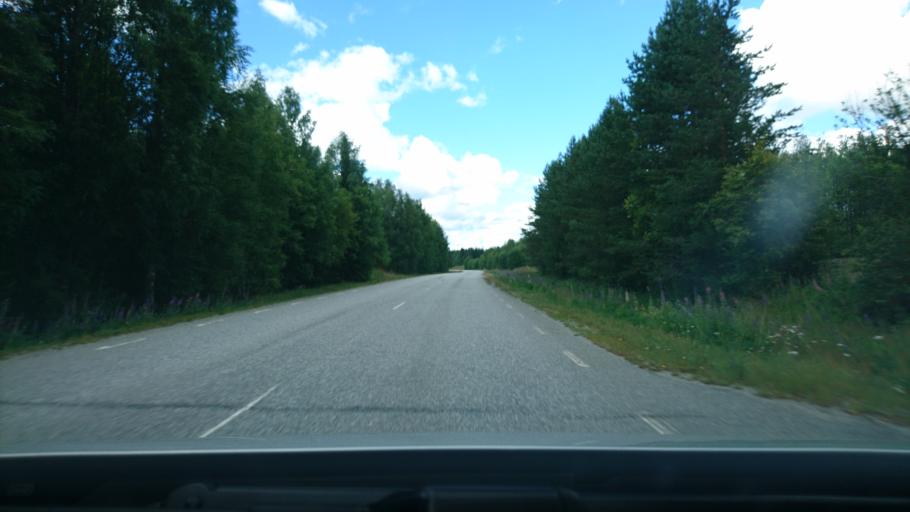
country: SE
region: Vaesterbotten
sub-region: Asele Kommun
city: Asele
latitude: 63.9735
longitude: 17.2632
